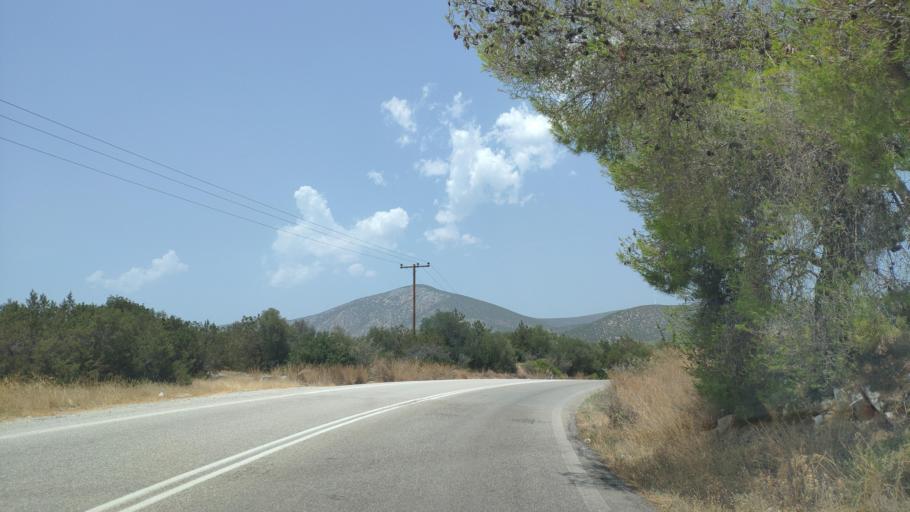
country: GR
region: Peloponnese
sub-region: Nomos Argolidos
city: Koilas
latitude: 37.4240
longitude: 23.1522
